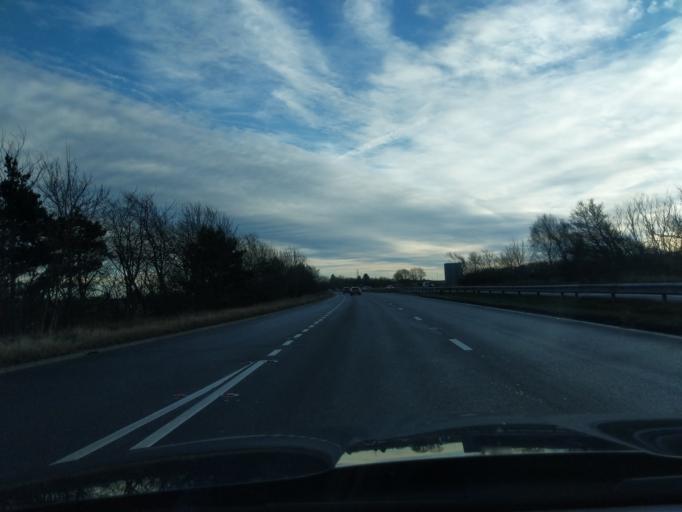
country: GB
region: England
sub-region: Northumberland
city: Seghill
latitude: 55.0434
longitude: -1.5492
